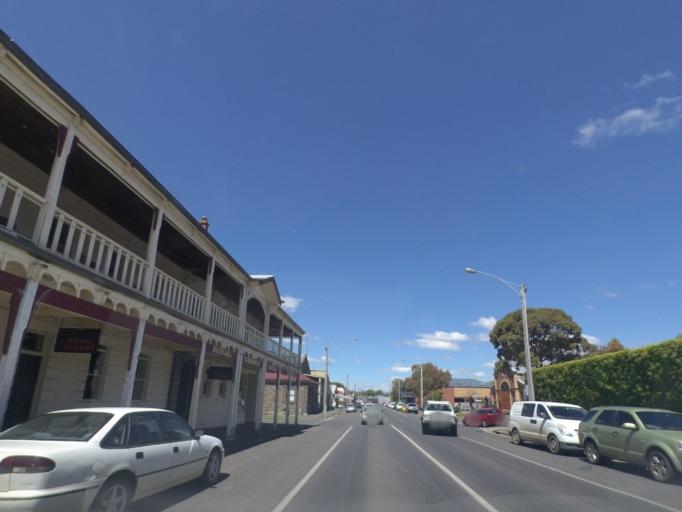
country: AU
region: Victoria
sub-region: Mount Alexander
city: Castlemaine
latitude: -37.2443
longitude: 144.4511
